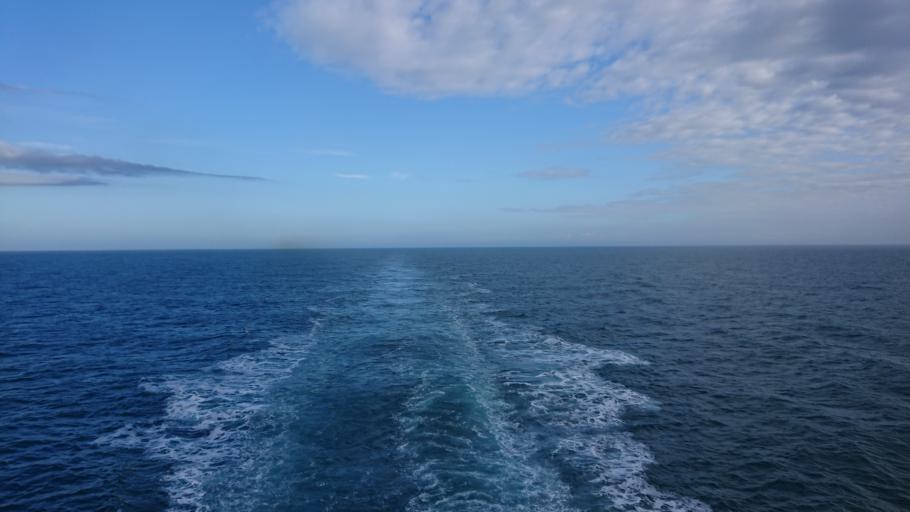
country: GB
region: Wales
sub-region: Pembrokeshire
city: Saint David's
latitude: 52.1339
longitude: -5.6125
